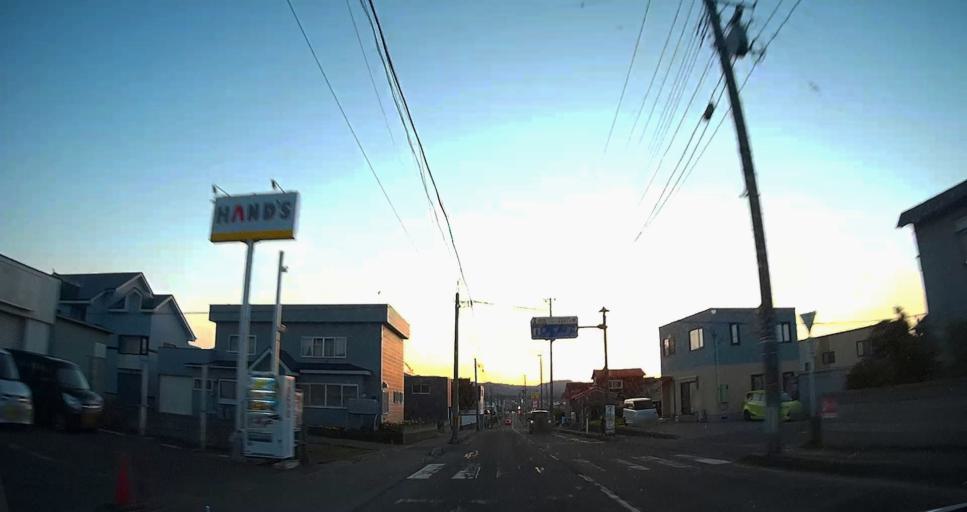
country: JP
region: Aomori
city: Misawa
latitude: 40.8686
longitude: 141.1207
